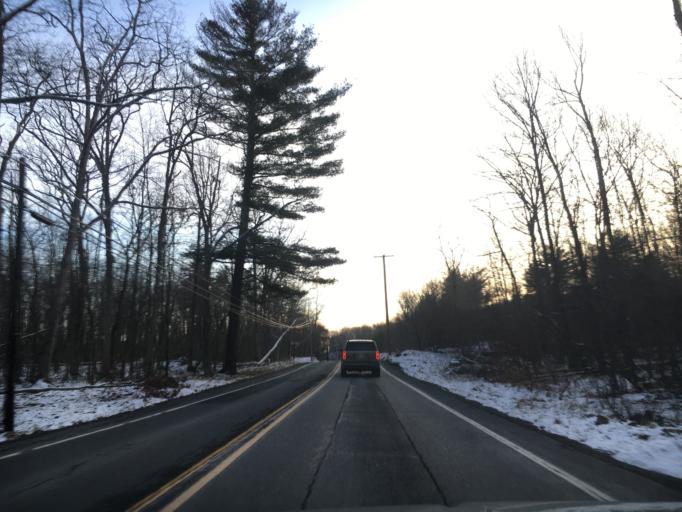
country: US
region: Pennsylvania
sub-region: Pike County
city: Saw Creek
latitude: 41.1001
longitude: -75.0978
